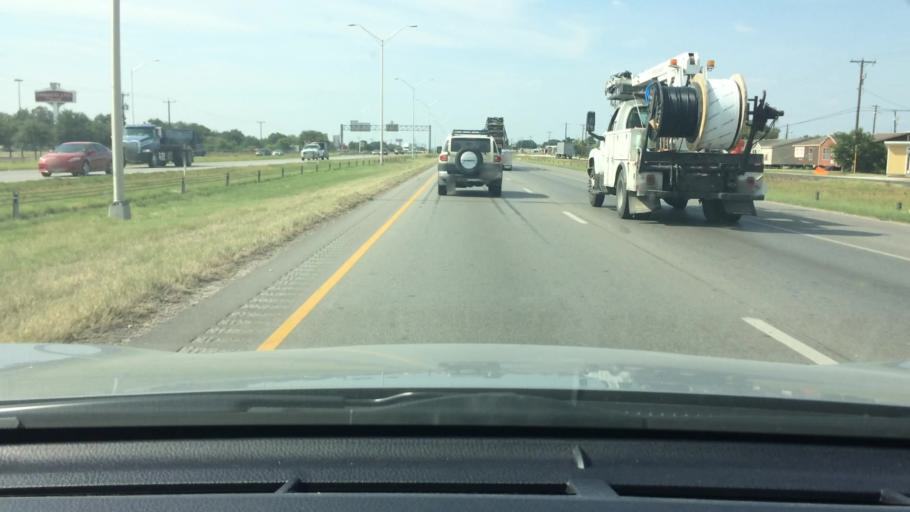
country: US
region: Texas
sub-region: Bexar County
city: China Grove
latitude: 29.4064
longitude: -98.3892
